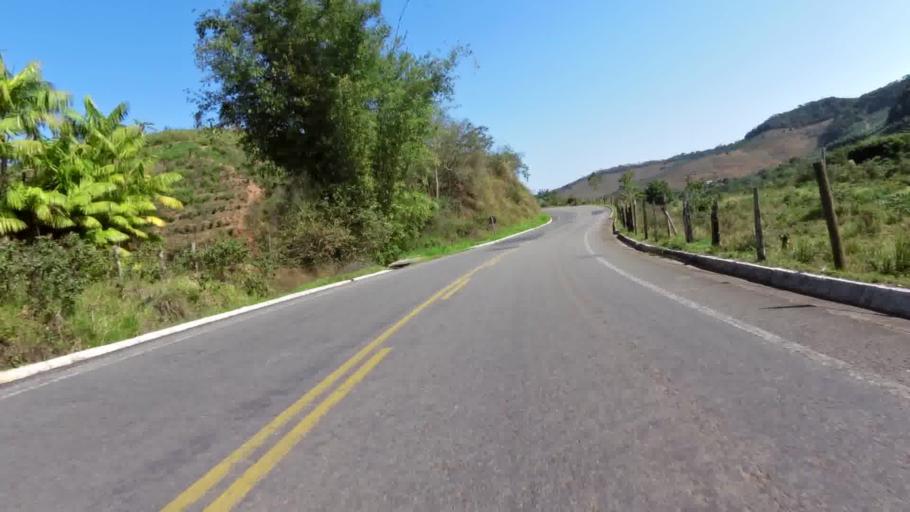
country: BR
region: Espirito Santo
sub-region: Alfredo Chaves
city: Alfredo Chaves
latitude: -20.5264
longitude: -40.7795
